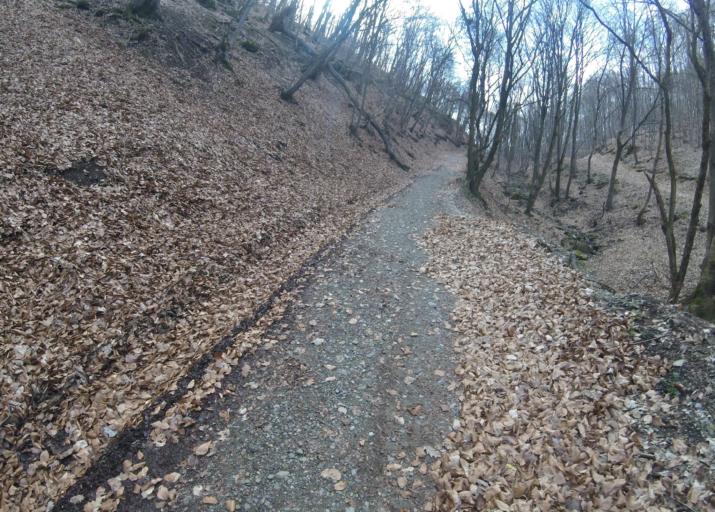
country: HU
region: Heves
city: Belapatfalva
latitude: 48.0356
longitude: 20.3536
